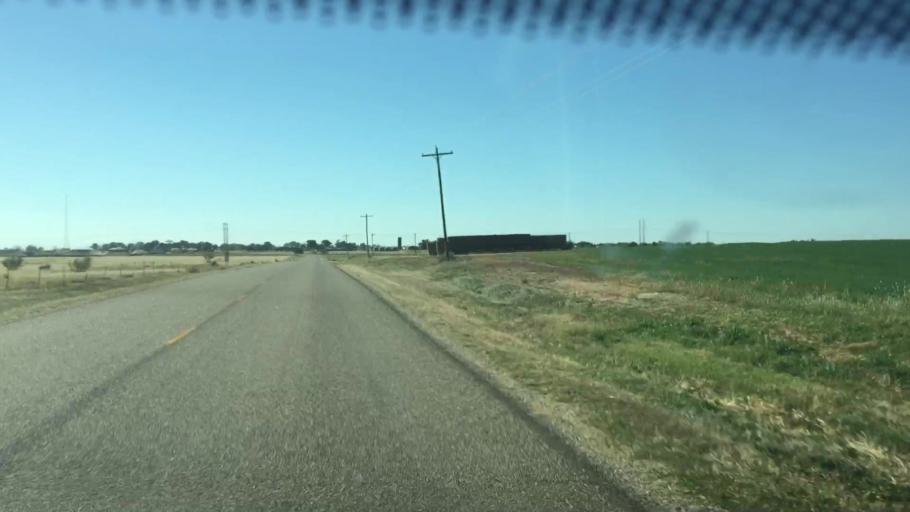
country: US
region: Colorado
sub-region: Prowers County
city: Lamar
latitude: 38.1160
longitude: -102.6017
